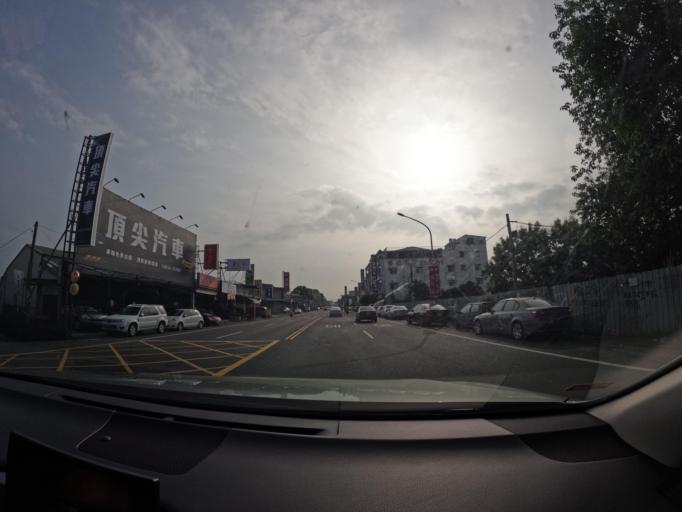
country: TW
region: Taiwan
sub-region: Chiayi
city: Jiayi Shi
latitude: 23.4512
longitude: 120.4683
